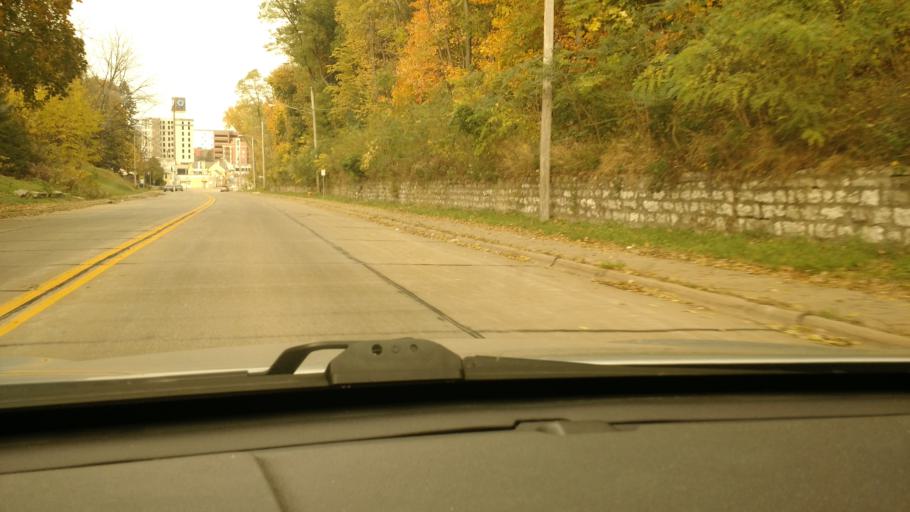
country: US
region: Illinois
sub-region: Rock Island County
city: Moline
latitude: 41.5011
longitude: -90.5156
